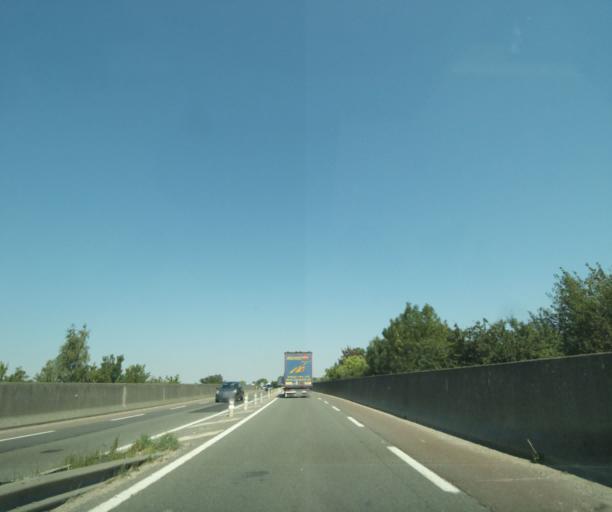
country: FR
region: Champagne-Ardenne
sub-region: Departement de la Haute-Marne
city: Saint-Dizier
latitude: 48.6380
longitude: 4.9201
